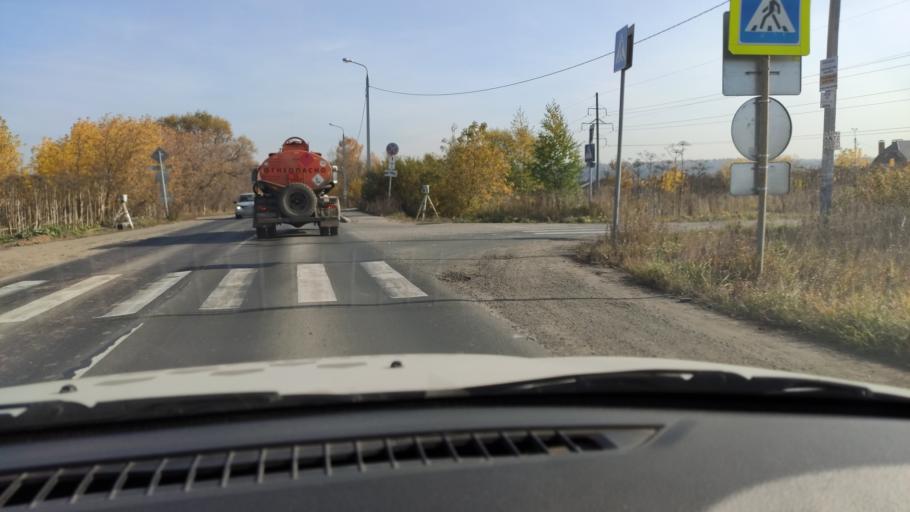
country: RU
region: Perm
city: Perm
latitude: 58.0390
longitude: 56.3904
